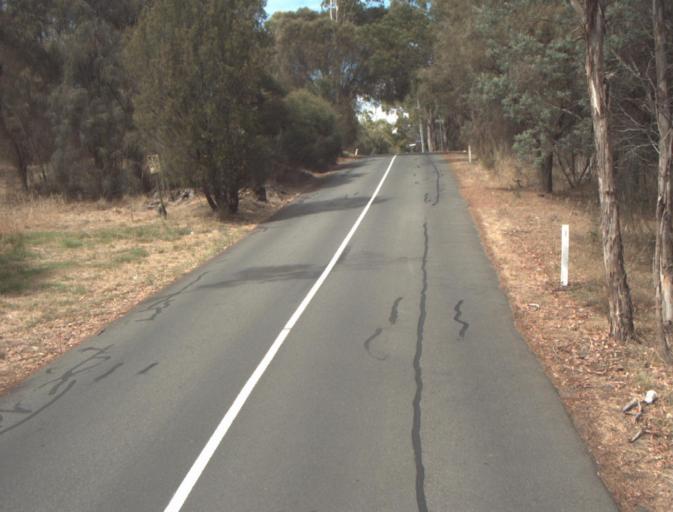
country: AU
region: Tasmania
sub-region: Launceston
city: West Launceston
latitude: -41.4510
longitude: 147.1191
